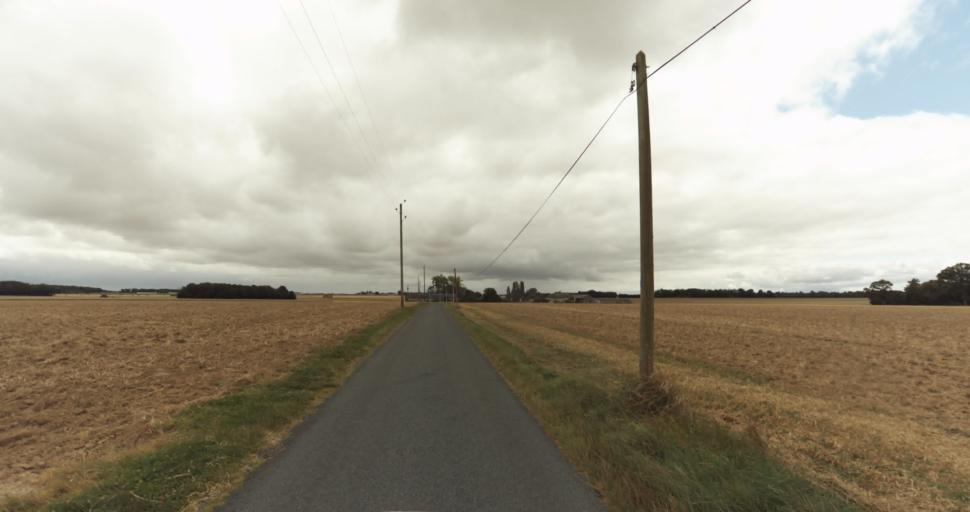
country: FR
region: Haute-Normandie
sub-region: Departement de l'Eure
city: Evreux
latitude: 48.9072
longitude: 1.2079
